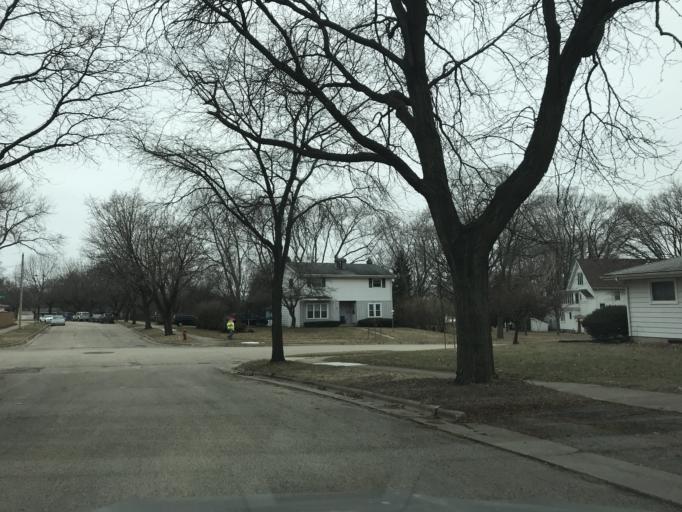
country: US
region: Wisconsin
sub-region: Dane County
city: Monona
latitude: 43.0980
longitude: -89.2995
